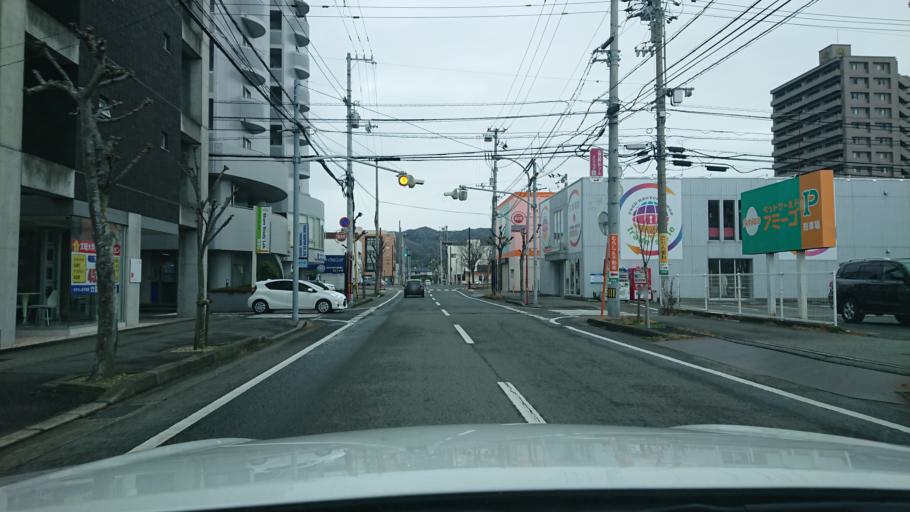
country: JP
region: Tokushima
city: Tokushima-shi
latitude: 34.0533
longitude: 134.5542
